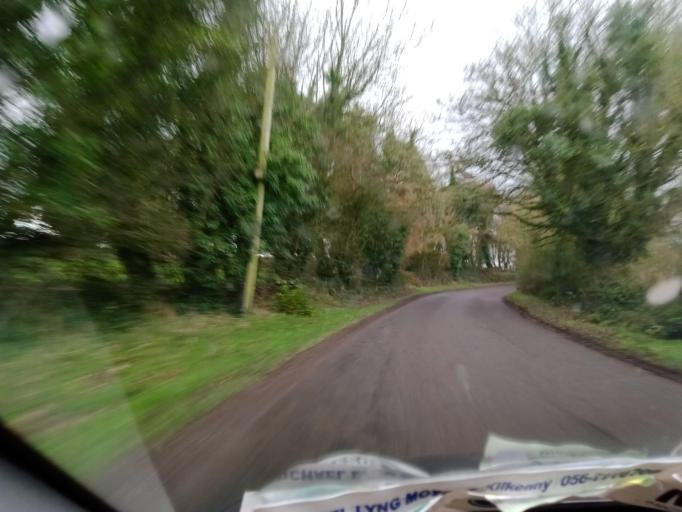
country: IE
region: Munster
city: Fethard
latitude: 52.5517
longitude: -7.7613
